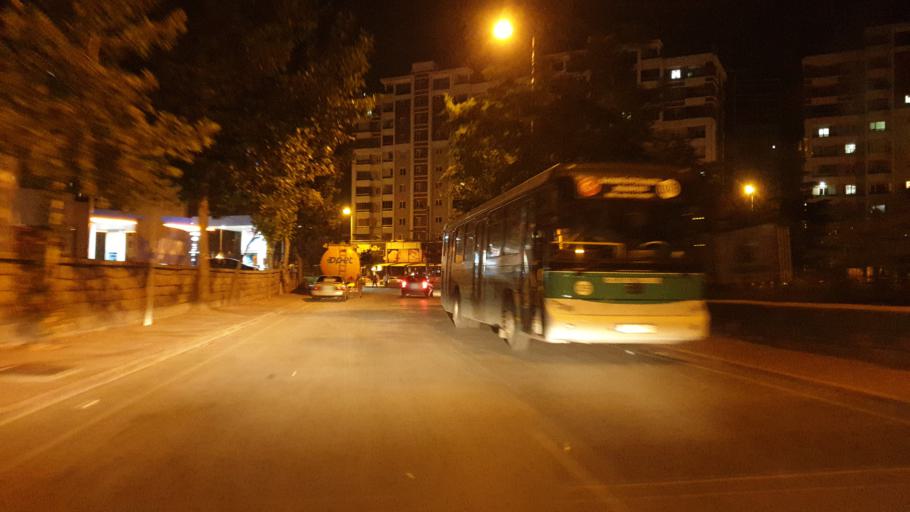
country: TR
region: Kayseri
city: Talas
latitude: 38.6942
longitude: 35.5421
